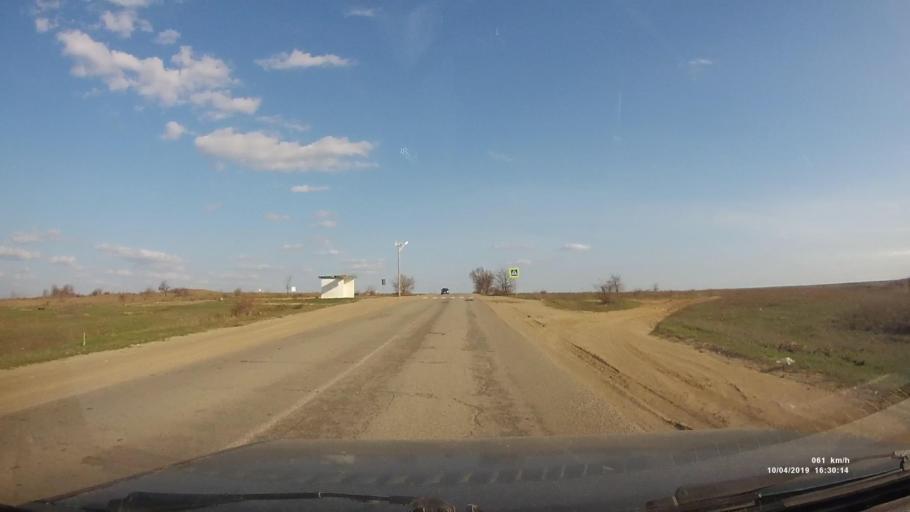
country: RU
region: Rostov
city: Staraya Stanitsa
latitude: 48.2633
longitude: 40.3635
